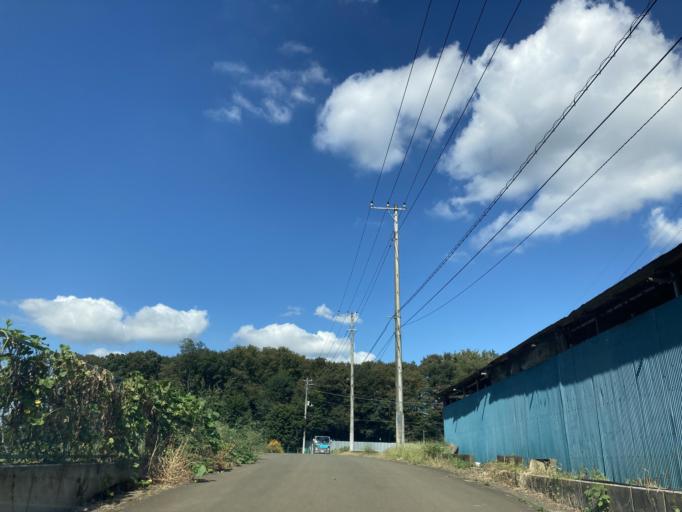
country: JP
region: Saitama
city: Tokorozawa
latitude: 35.8056
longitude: 139.5013
